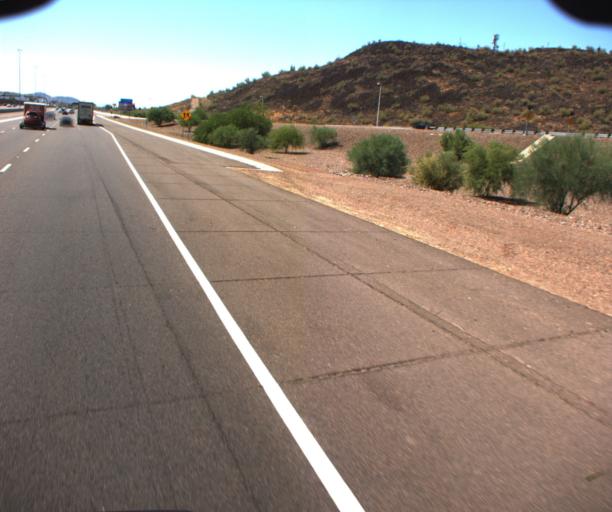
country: US
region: Arizona
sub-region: Maricopa County
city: Anthem
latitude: 33.6996
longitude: -112.1148
